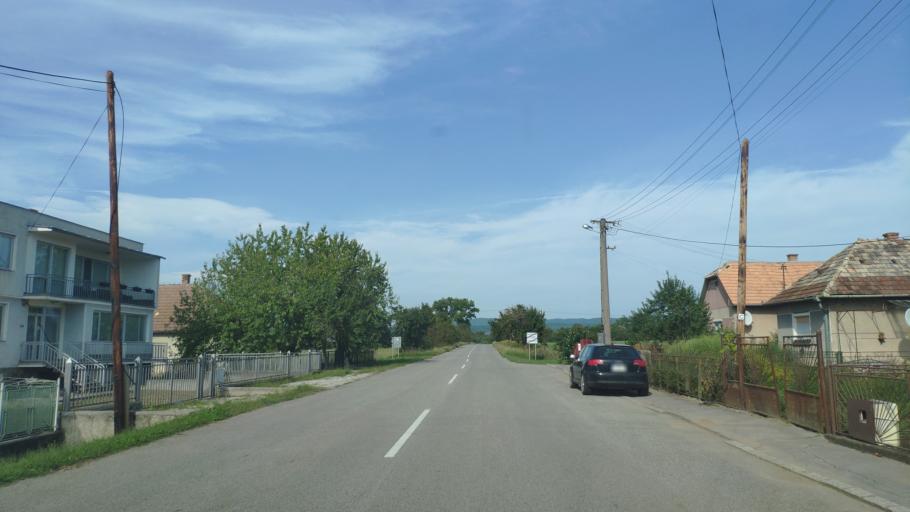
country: HU
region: Borsod-Abauj-Zemplen
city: Putnok
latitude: 48.4767
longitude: 20.3535
